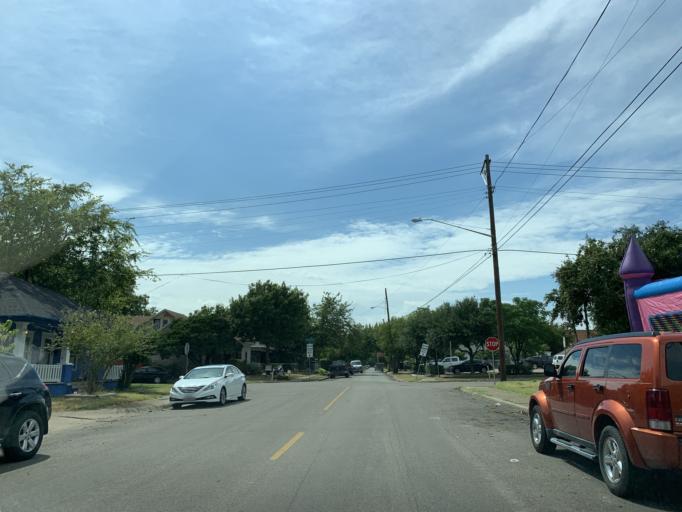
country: US
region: Texas
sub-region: Dallas County
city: Dallas
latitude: 32.7424
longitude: -96.8353
